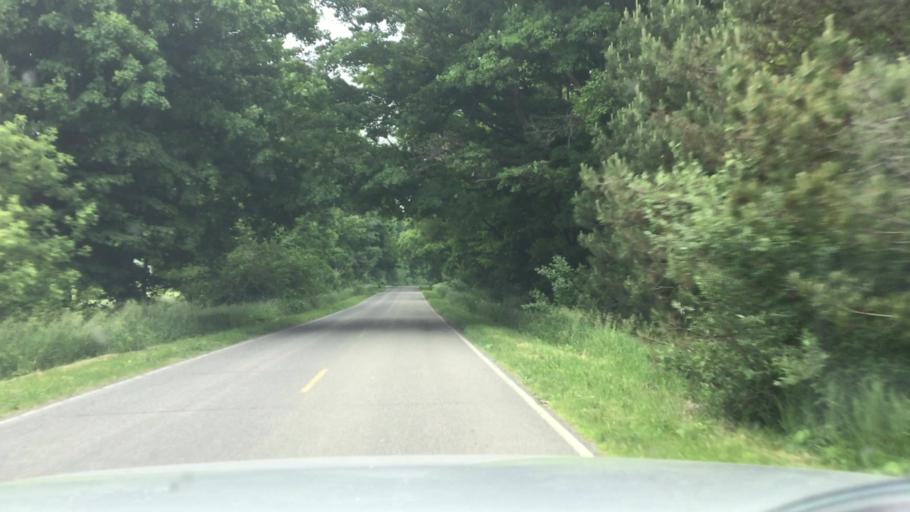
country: US
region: Michigan
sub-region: Shiawassee County
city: Durand
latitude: 42.7835
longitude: -84.0013
